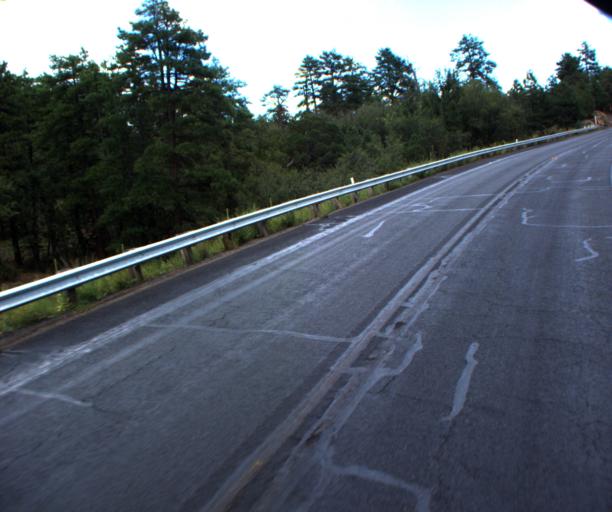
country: US
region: Arizona
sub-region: Gila County
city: Pine
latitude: 34.5150
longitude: -111.4896
